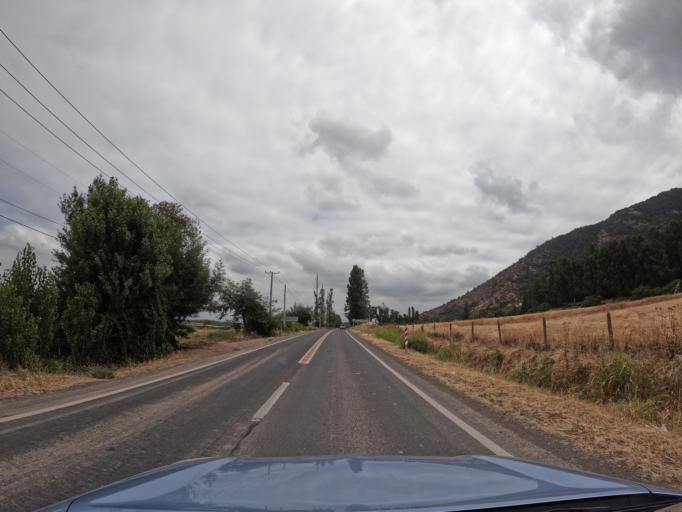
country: CL
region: Maule
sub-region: Provincia de Curico
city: Teno
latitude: -34.7821
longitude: -71.2302
